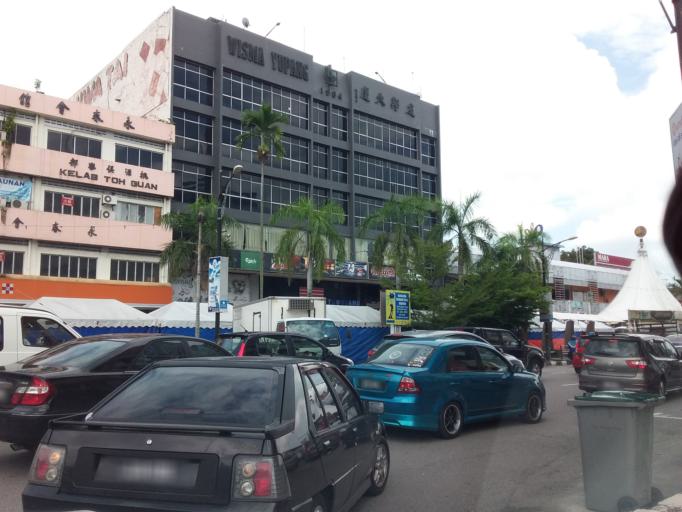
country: MY
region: Johor
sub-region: Daerah Batu Pahat
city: Batu Pahat
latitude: 1.8487
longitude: 102.9320
